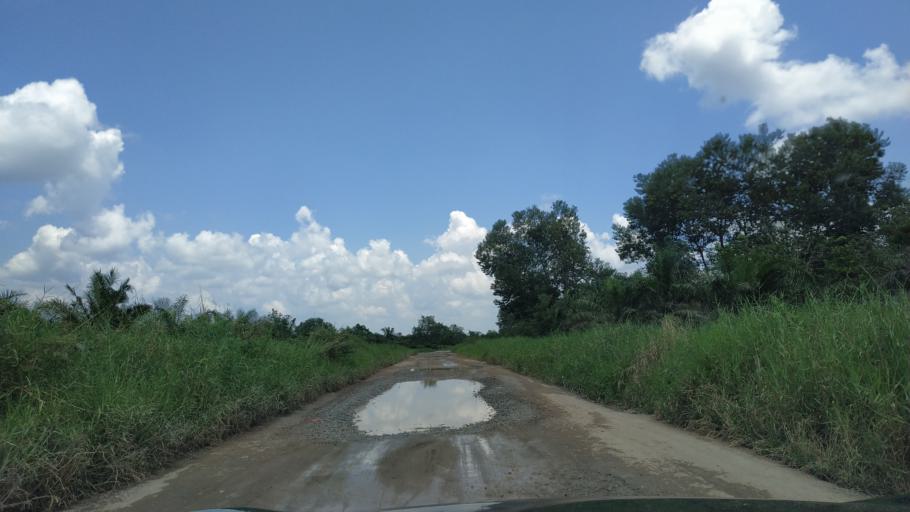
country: ID
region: Riau
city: Pangkalanbunut
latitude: 0.1950
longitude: 102.3866
